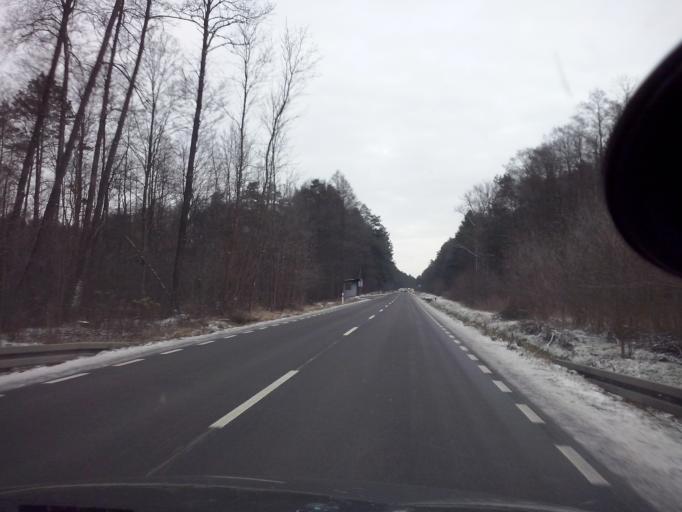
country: PL
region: Lublin Voivodeship
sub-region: Powiat bilgorajski
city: Bilgoraj
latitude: 50.5594
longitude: 22.7678
